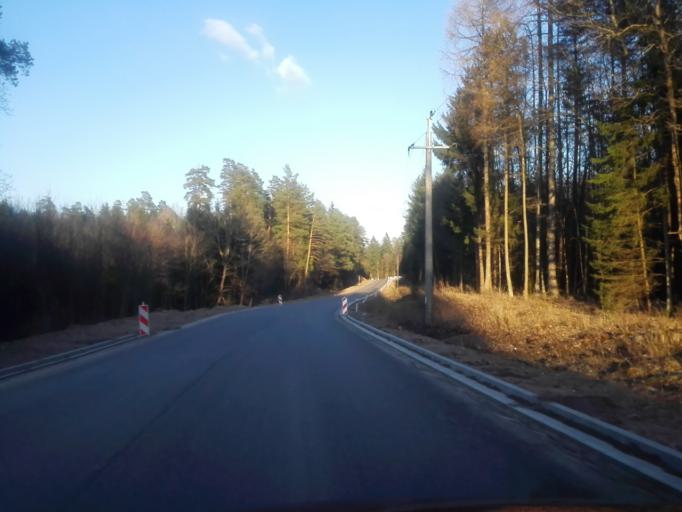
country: PL
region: Podlasie
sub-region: Suwalki
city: Suwalki
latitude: 54.0741
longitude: 23.0360
